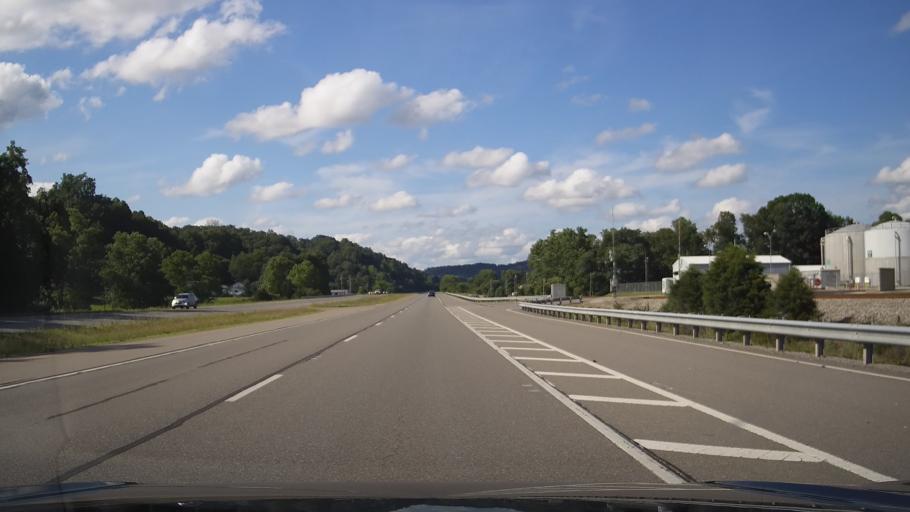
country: US
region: Kentucky
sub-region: Lawrence County
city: Louisa
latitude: 38.1919
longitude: -82.6059
